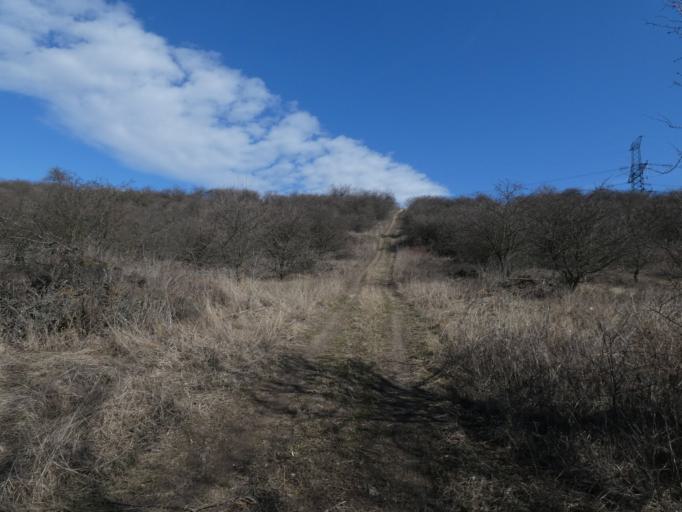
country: HU
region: Pest
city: Pecel
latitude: 47.5152
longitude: 19.3402
